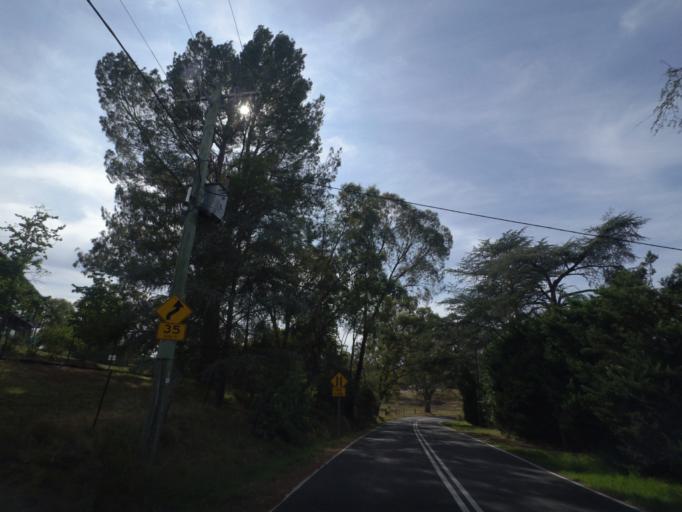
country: AU
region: Victoria
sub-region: Banyule
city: Viewbank
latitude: -37.7382
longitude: 145.1038
